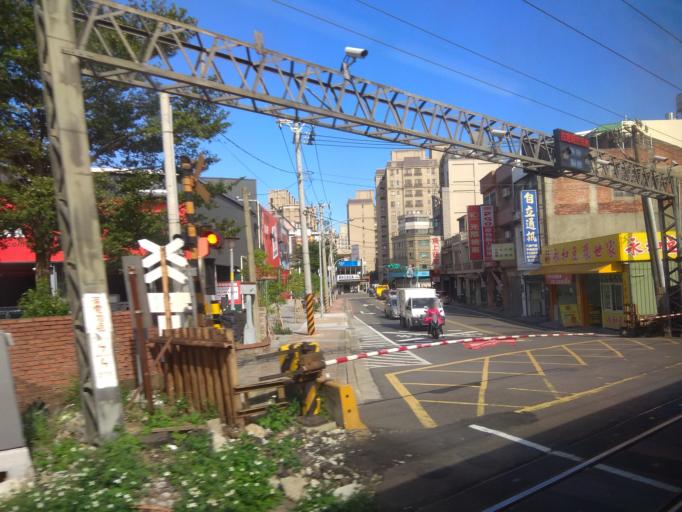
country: TW
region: Taiwan
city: Taoyuan City
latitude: 24.9686
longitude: 121.2507
